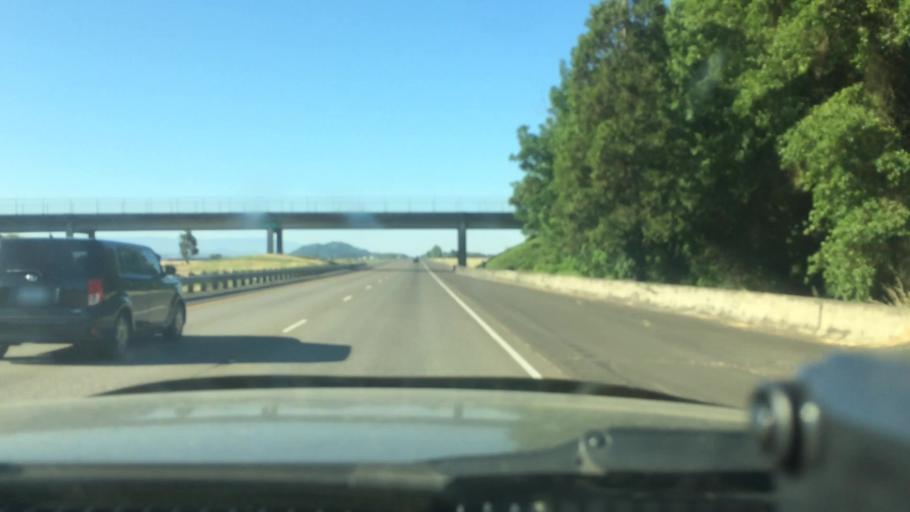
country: US
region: Oregon
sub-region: Linn County
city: Tangent
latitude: 44.5058
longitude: -123.0619
